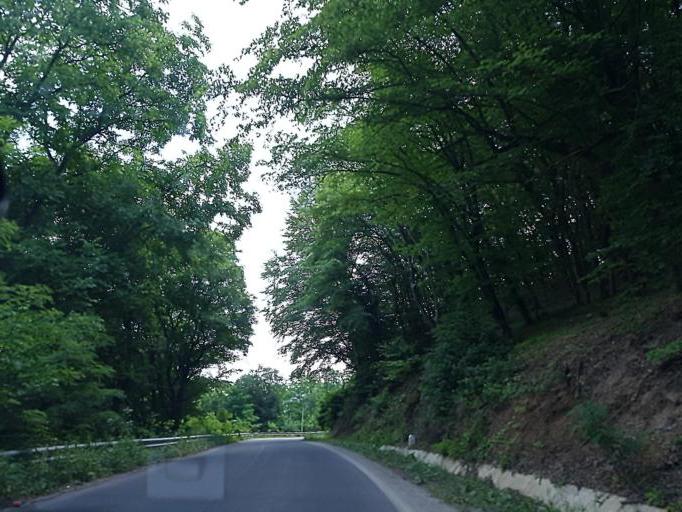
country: RO
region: Sibiu
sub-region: Comuna Seica Mare
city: Seica Mare
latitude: 46.0388
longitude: 24.1592
